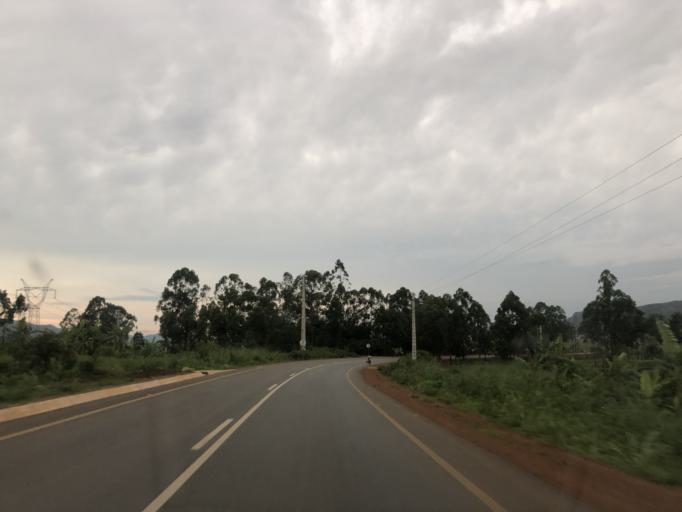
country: AO
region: Cuanza Sul
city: Uacu Cungo
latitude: -11.3341
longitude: 15.1017
